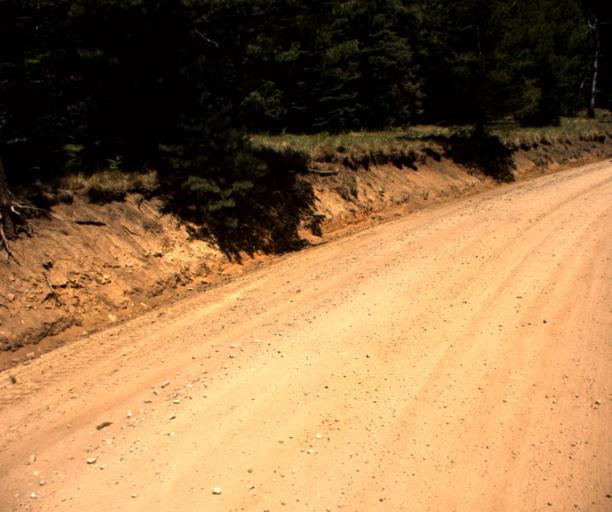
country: US
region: Arizona
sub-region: Graham County
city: Swift Trail Junction
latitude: 32.6701
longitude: -109.8779
